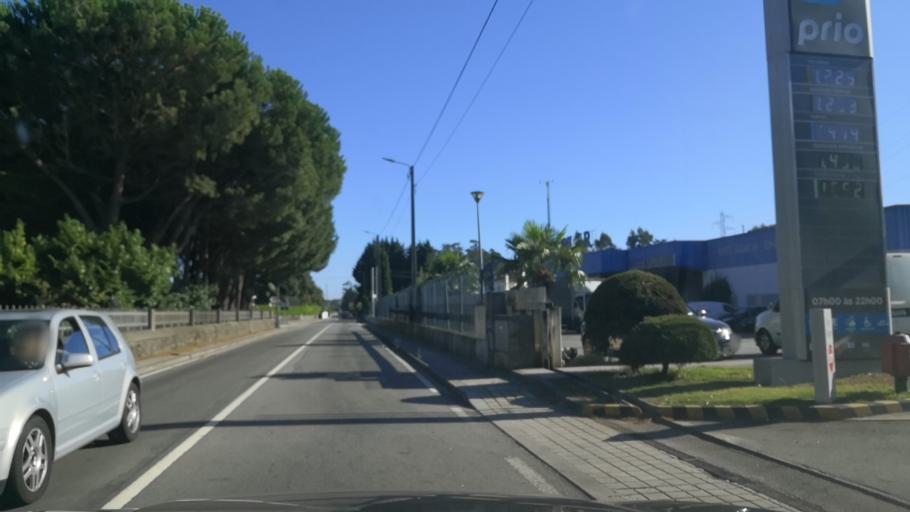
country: PT
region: Porto
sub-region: Santo Tirso
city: Sao Miguel do Couto
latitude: 41.2978
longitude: -8.4710
